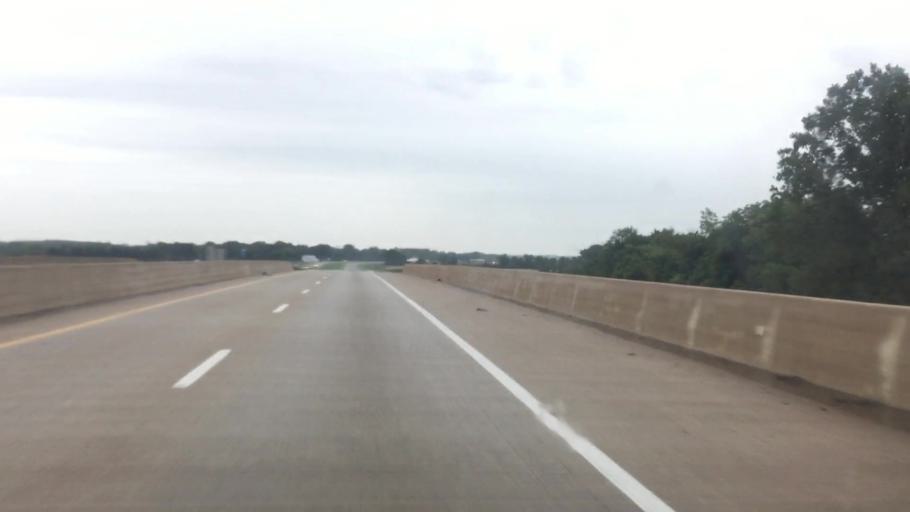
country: US
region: Ohio
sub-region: Henry County
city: Liberty Center
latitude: 41.4235
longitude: -84.0243
